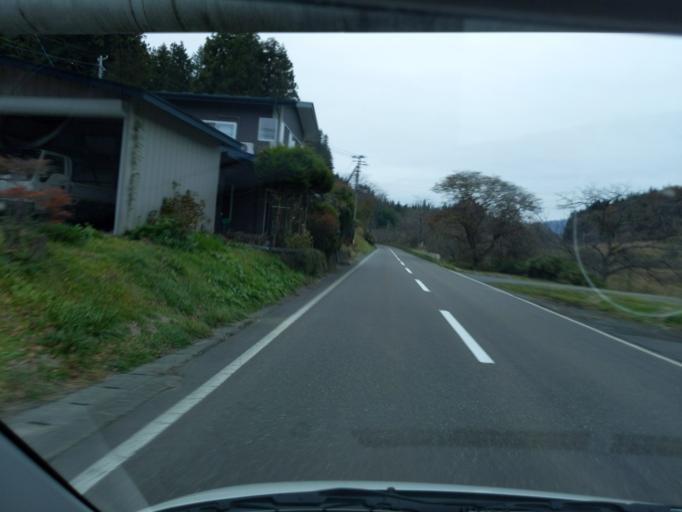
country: JP
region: Iwate
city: Kitakami
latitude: 39.2300
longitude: 141.2865
